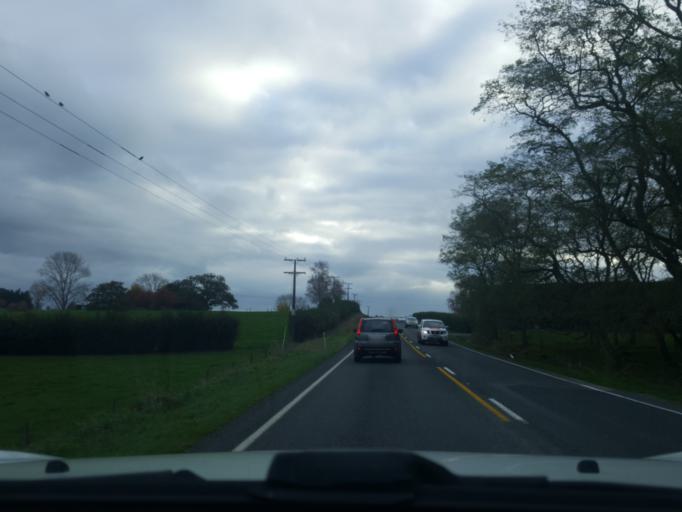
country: NZ
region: Waikato
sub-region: Matamata-Piako District
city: Matamata
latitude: -37.8903
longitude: 175.7844
